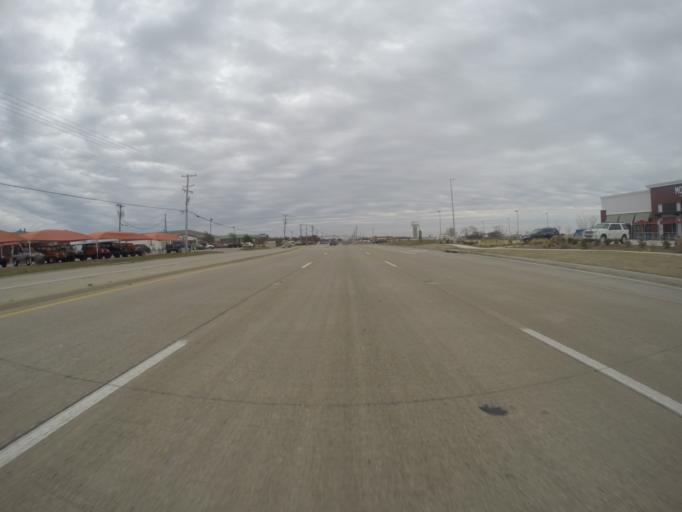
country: US
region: Texas
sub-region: Collin County
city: Saint Paul
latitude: 33.0417
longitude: -96.5648
